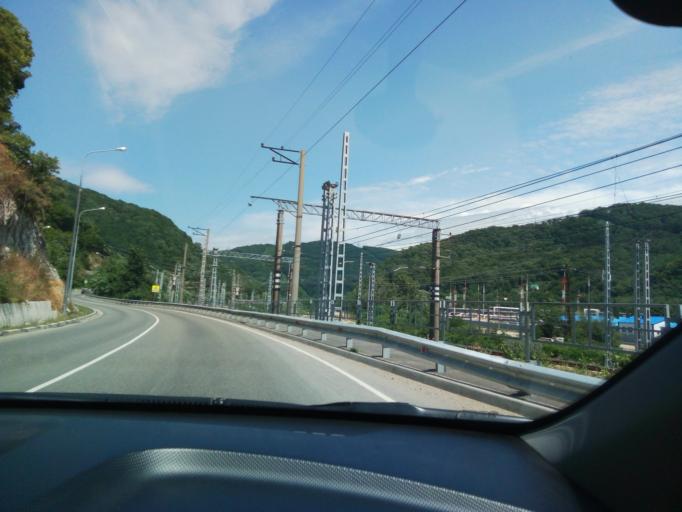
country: RU
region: Krasnodarskiy
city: Tuapse
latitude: 44.1189
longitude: 39.1197
